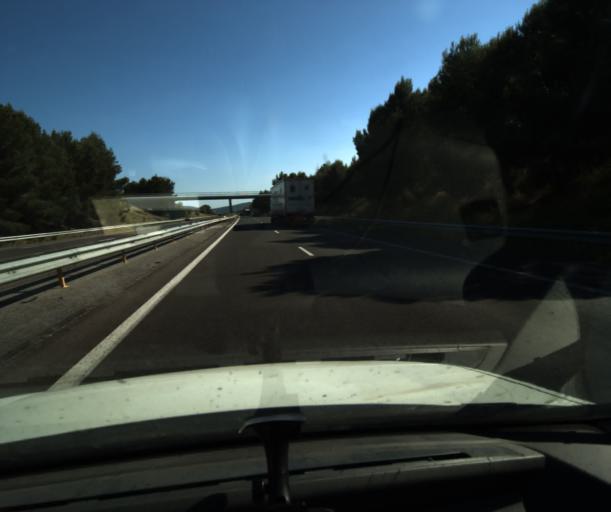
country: FR
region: Languedoc-Roussillon
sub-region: Departement des Pyrenees-Orientales
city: Villemolaque
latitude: 42.5713
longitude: 2.8438
